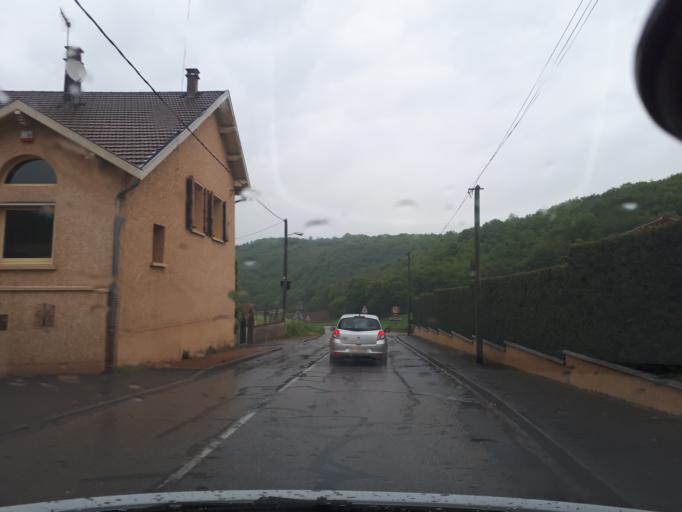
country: FR
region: Rhone-Alpes
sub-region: Departement de l'Isere
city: Frontonas
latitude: 45.6804
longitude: 5.2072
